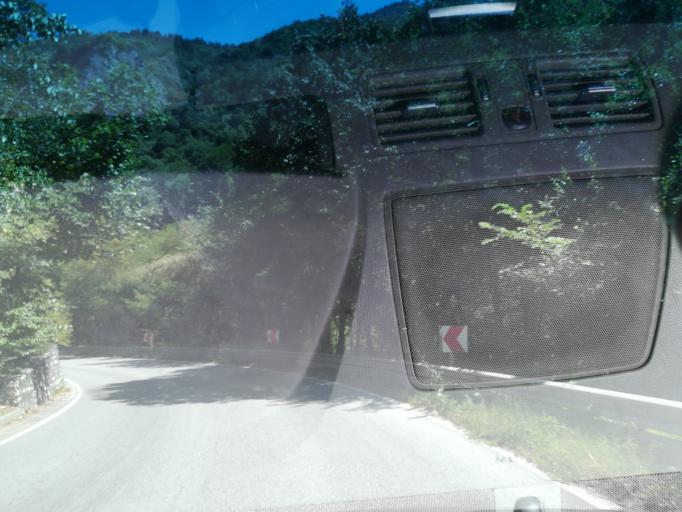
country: BG
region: Plovdiv
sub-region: Obshtina Luki
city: Luki
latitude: 41.9256
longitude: 24.8395
